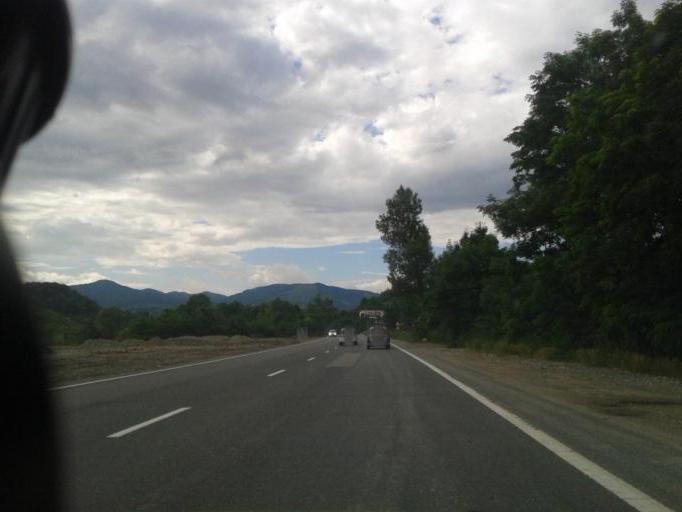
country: RO
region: Prahova
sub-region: Oras Breaza
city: Breaza de Sus
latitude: 45.2068
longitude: 25.6599
